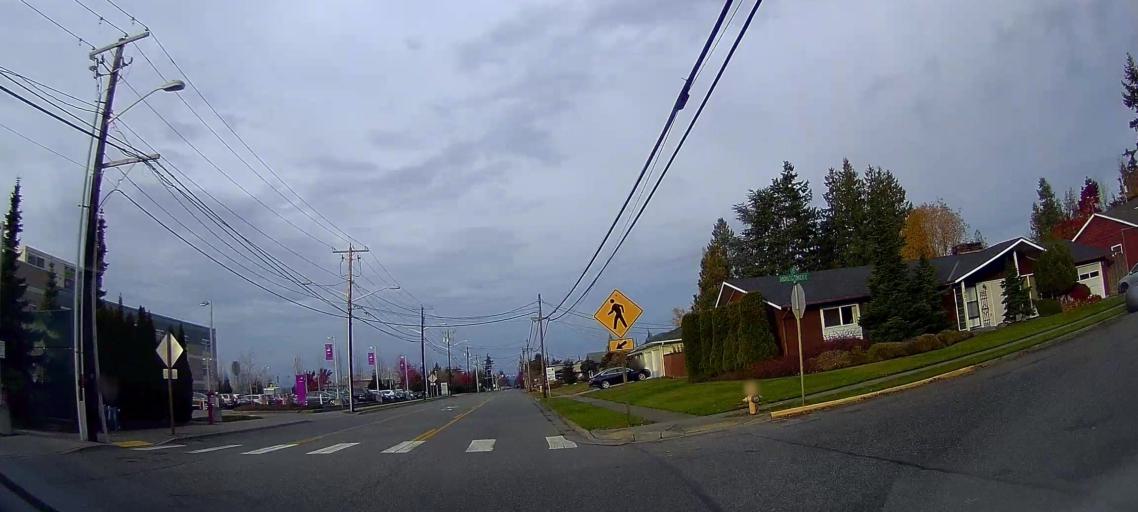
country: US
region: Washington
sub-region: Skagit County
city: Mount Vernon
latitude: 48.4182
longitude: -122.3229
